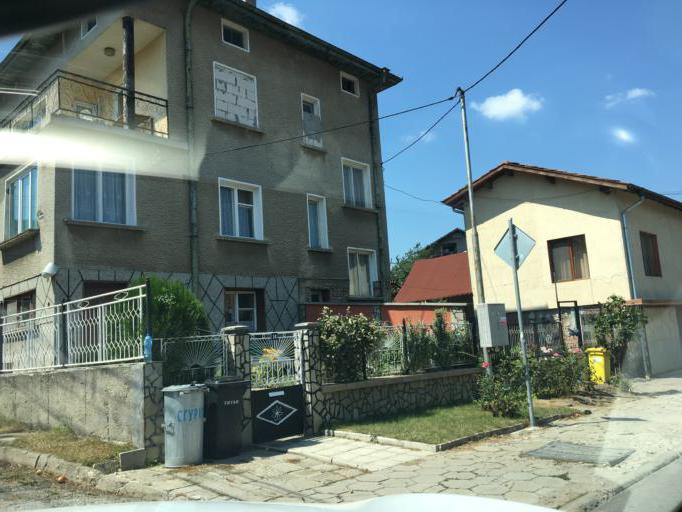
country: BG
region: Sofiya
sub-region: Obshtina Elin Pelin
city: Elin Pelin
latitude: 42.6061
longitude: 23.4705
